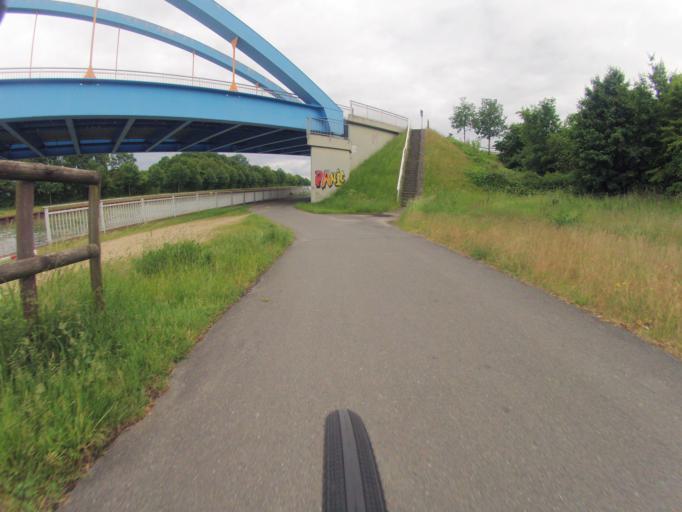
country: DE
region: North Rhine-Westphalia
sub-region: Regierungsbezirk Munster
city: Birgte
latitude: 52.2192
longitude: 7.6777
